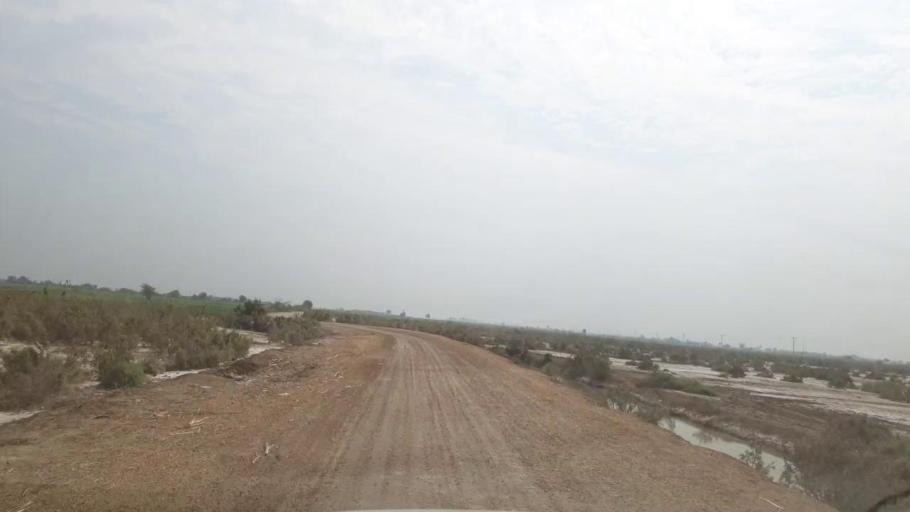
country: PK
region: Sindh
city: Mirpur Khas
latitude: 25.5464
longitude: 69.1254
